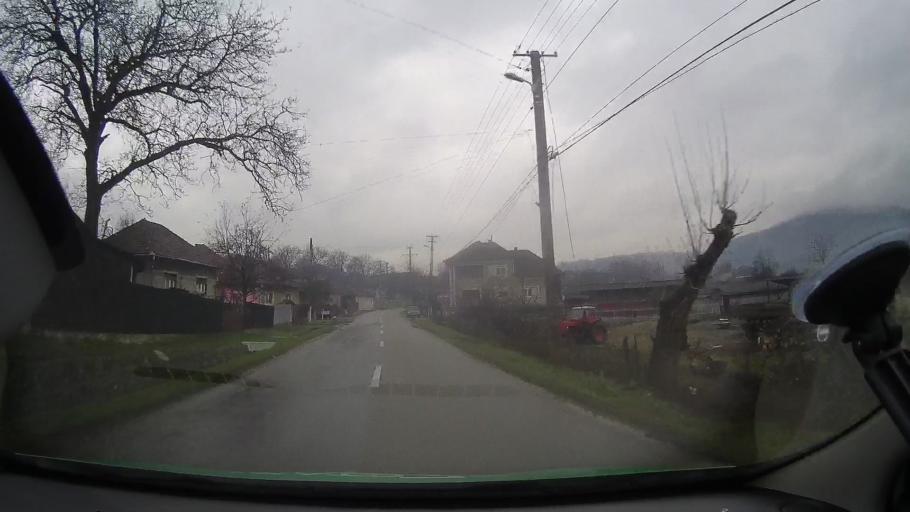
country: RO
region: Arad
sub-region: Comuna Gurahont
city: Gurahont
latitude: 46.2660
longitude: 22.3424
